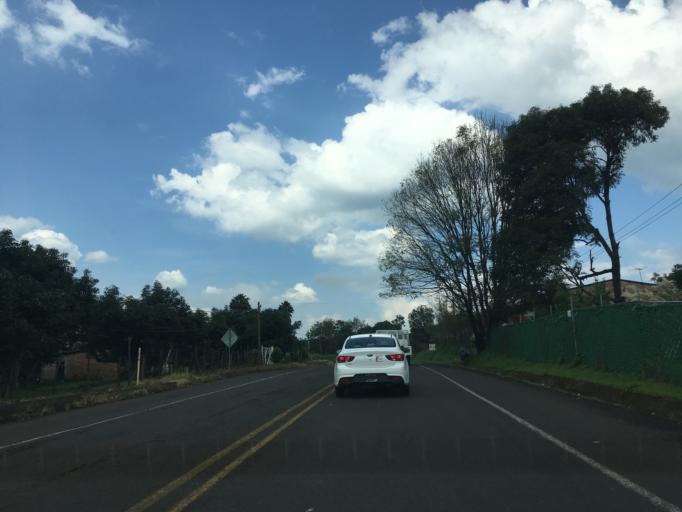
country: MX
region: Michoacan
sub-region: Tingueindin
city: Tingueindin
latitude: 19.7463
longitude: -102.4861
